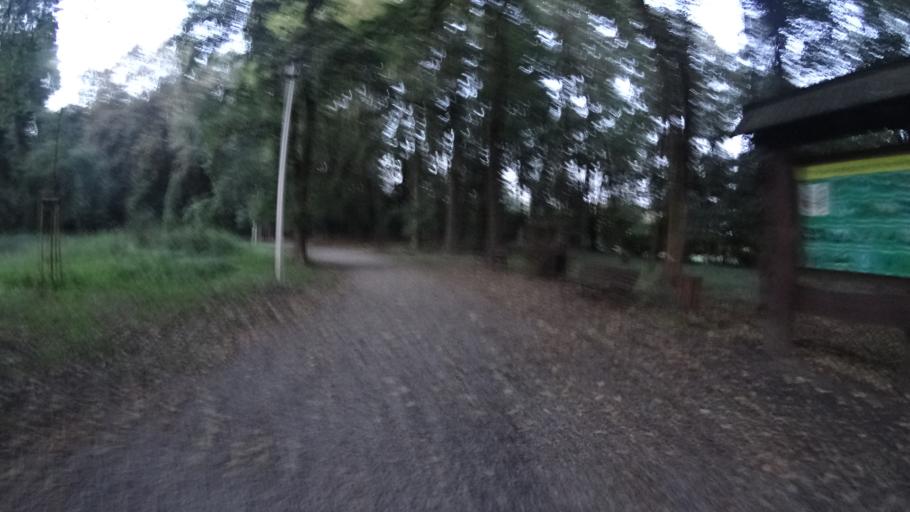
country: PL
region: Masovian Voivodeship
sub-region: Powiat warszawski zachodni
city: Ozarow Mazowiecki
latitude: 52.2151
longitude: 20.7754
